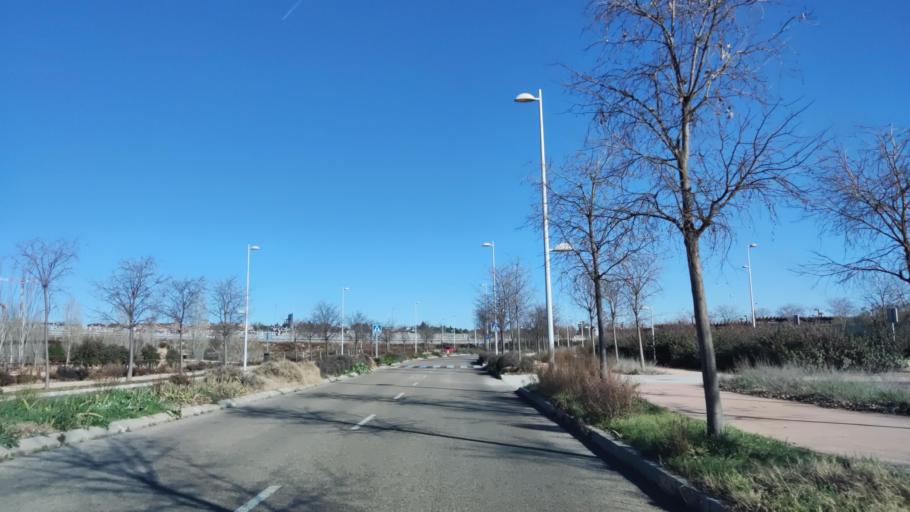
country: ES
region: Madrid
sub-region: Provincia de Madrid
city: Hortaleza
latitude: 40.4969
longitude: -3.6372
